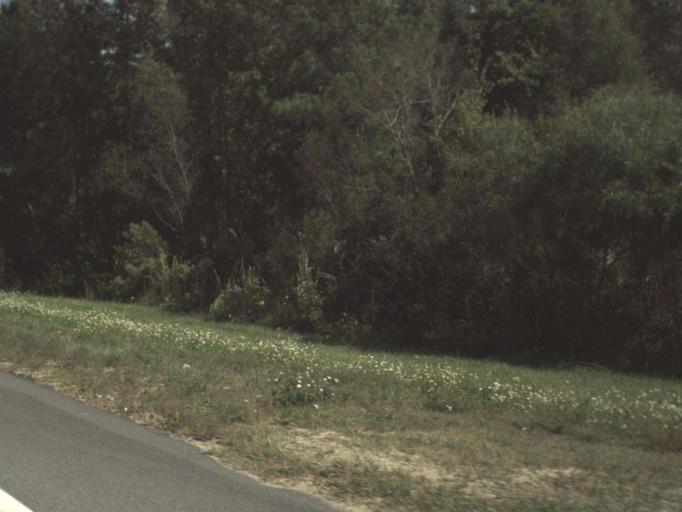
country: US
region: Florida
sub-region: Liberty County
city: Bristol
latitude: 30.3624
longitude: -84.8178
